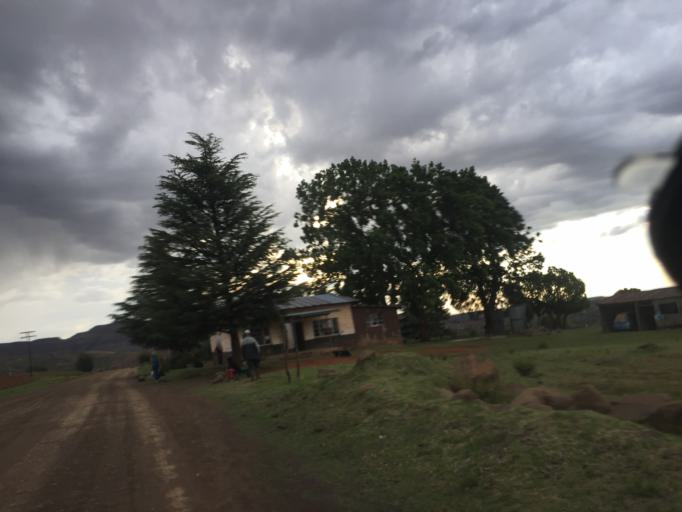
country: LS
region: Leribe
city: Leribe
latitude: -29.1548
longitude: 28.0369
